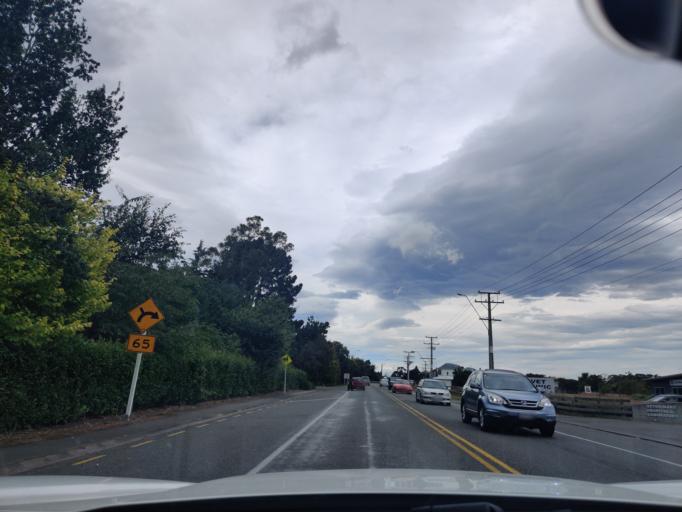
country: NZ
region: Wellington
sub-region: Masterton District
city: Masterton
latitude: -41.0162
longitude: 175.5356
